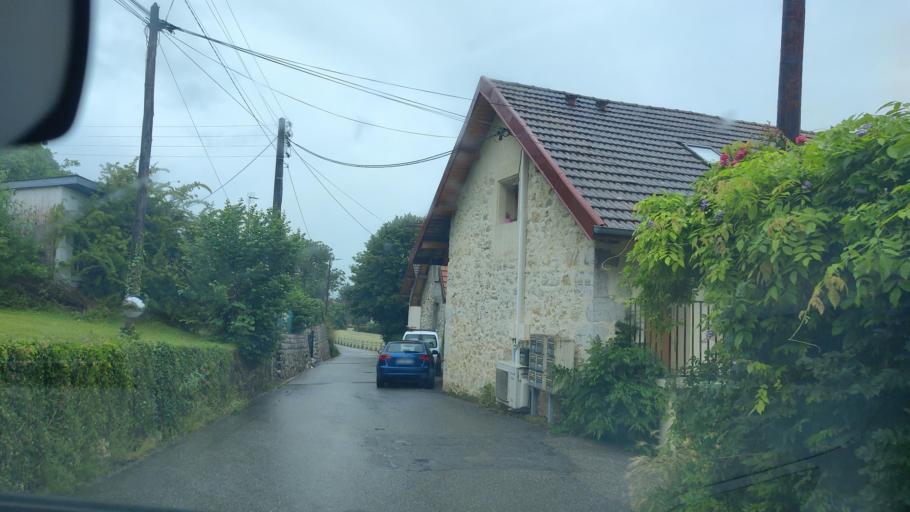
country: FR
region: Rhone-Alpes
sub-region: Departement de la Savoie
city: Chindrieux
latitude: 45.8167
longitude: 5.8525
